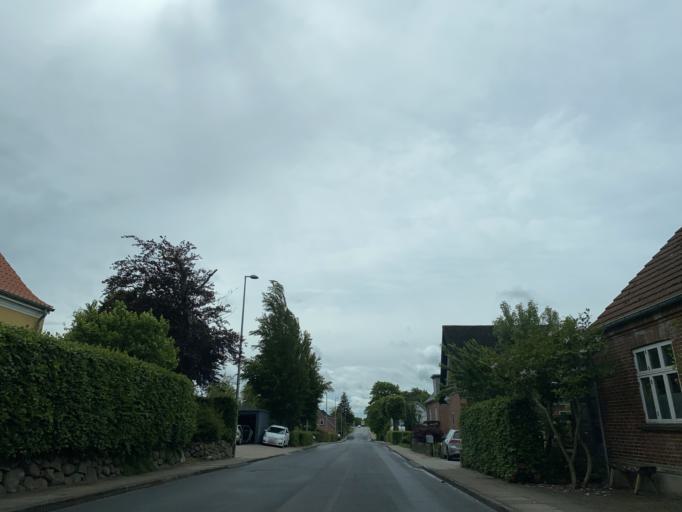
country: DK
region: Central Jutland
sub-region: Favrskov Kommune
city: Hammel
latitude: 56.2548
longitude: 9.8701
